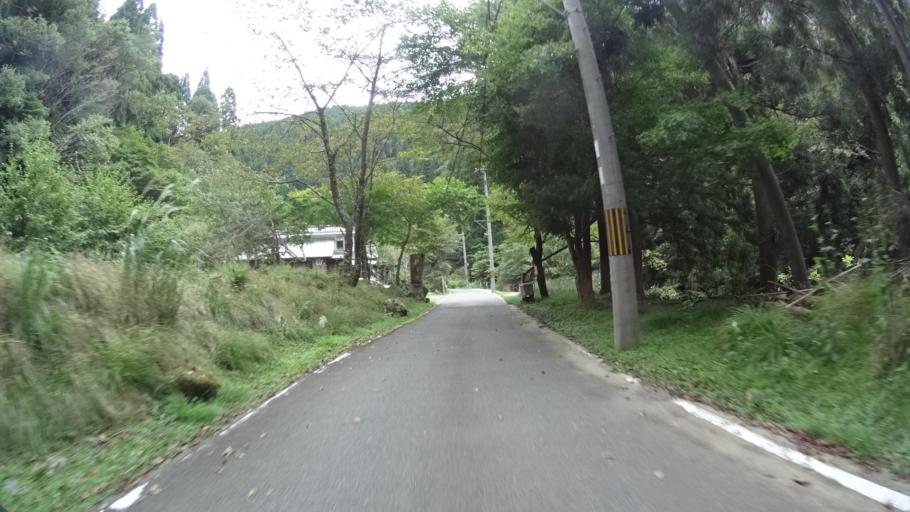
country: JP
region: Shiga Prefecture
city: Kitahama
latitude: 35.2350
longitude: 135.7856
